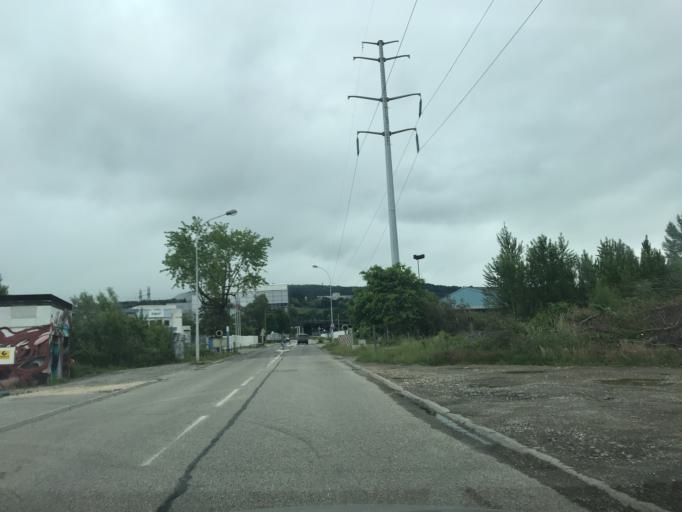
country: FR
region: Rhone-Alpes
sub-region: Departement de la Savoie
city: La Motte-Servolex
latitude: 45.5906
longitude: 5.8912
